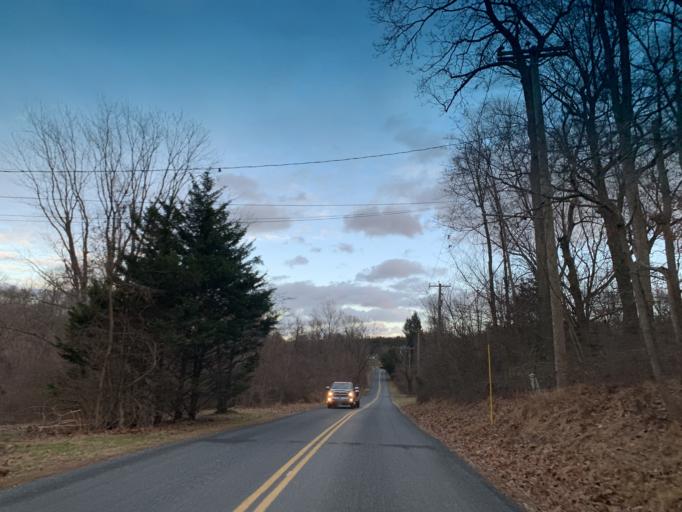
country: US
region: Pennsylvania
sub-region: York County
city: Susquehanna Trails
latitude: 39.6561
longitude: -76.2990
